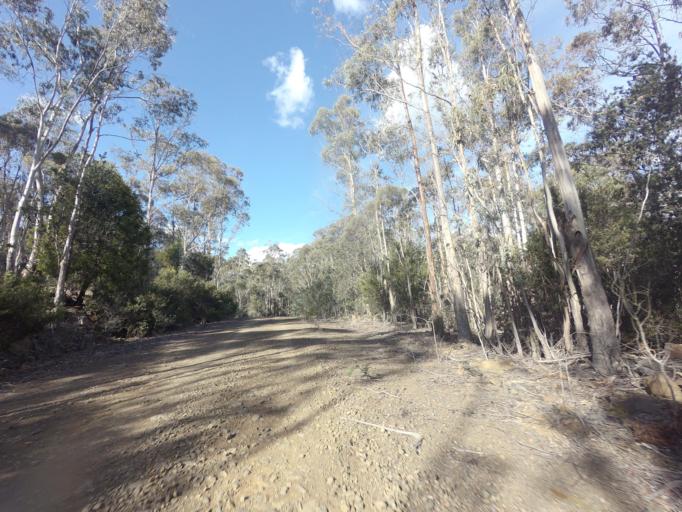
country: AU
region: Tasmania
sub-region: Break O'Day
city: St Helens
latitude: -41.8493
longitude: 148.0485
